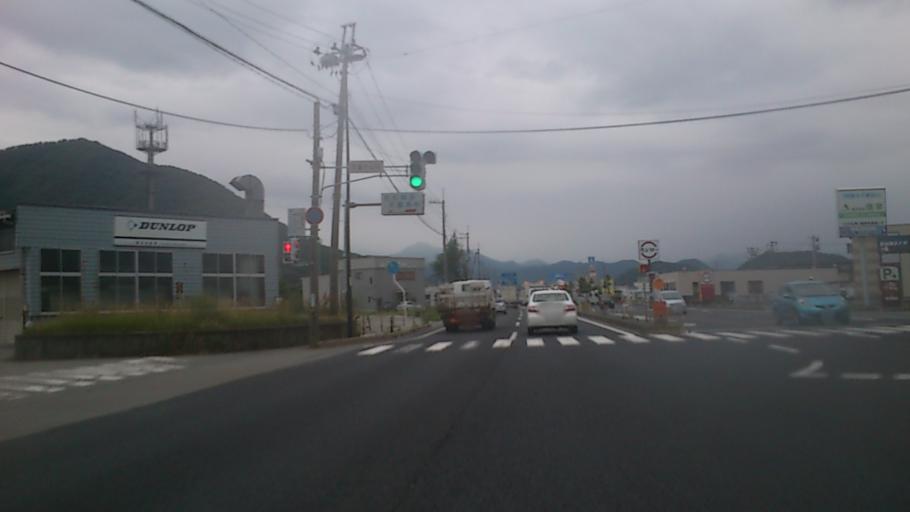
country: JP
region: Yamagata
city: Tendo
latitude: 38.3692
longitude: 140.3846
